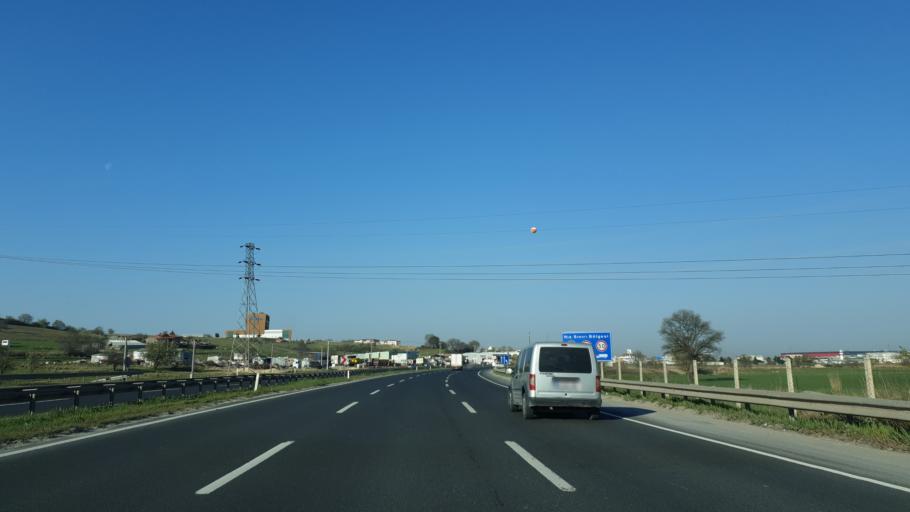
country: TR
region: Tekirdag
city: Cerkezkoey
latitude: 41.2663
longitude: 27.9541
